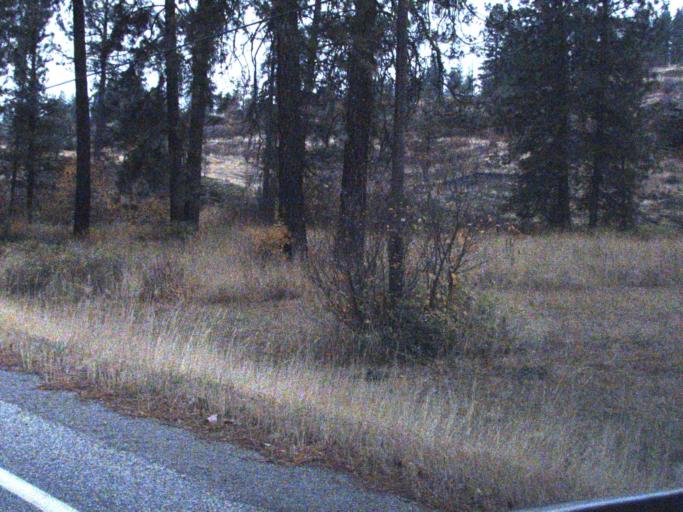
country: US
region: Washington
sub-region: Stevens County
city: Kettle Falls
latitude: 48.6535
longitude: -118.1139
